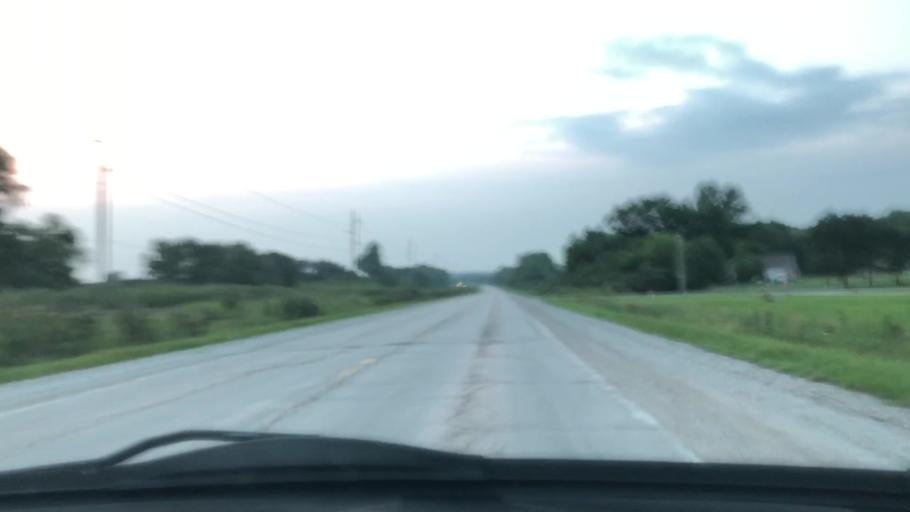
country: US
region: Iowa
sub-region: Johnson County
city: North Liberty
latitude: 41.7865
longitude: -91.6363
